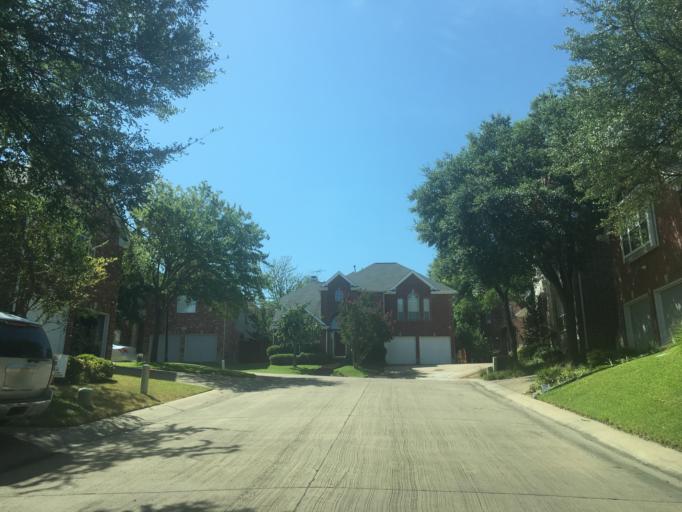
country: US
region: Texas
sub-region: Dallas County
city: Highland Park
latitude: 32.8697
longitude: -96.7301
